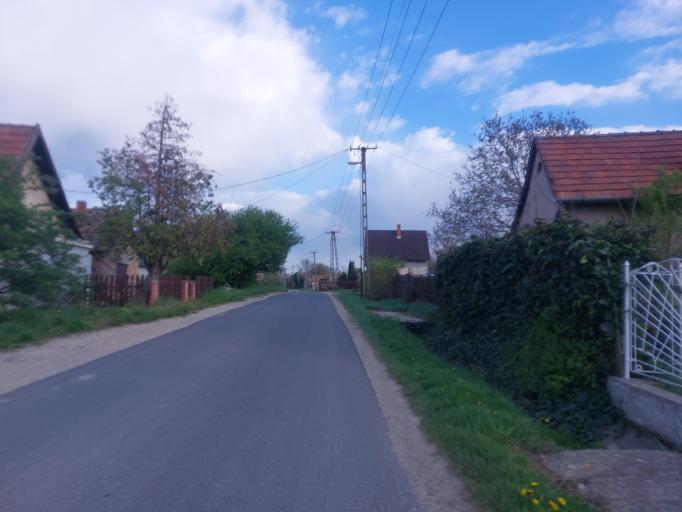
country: HU
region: Veszprem
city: Devecser
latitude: 47.1530
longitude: 17.3813
